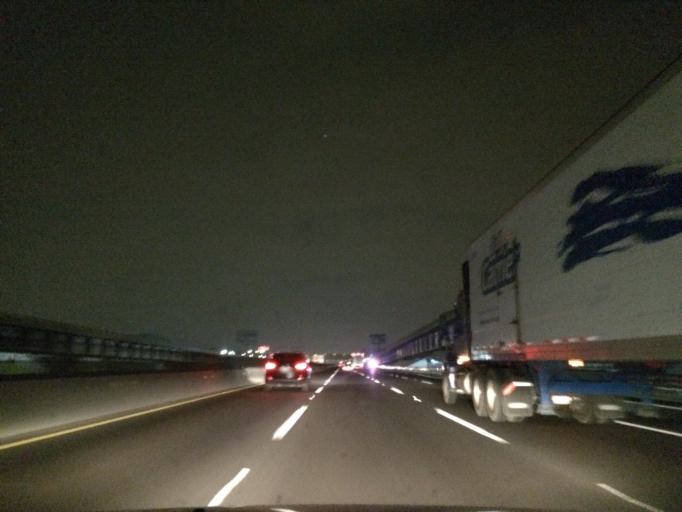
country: MX
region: Mexico
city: San Miguel Xico Viejo
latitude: 19.2943
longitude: -98.9235
